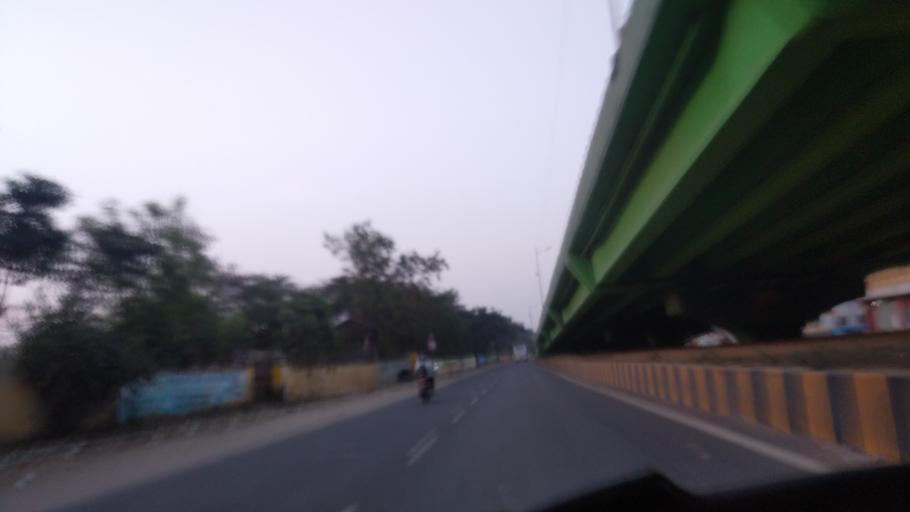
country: IN
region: Tamil Nadu
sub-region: Coimbatore
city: Coimbatore
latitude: 11.0118
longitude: 76.9677
